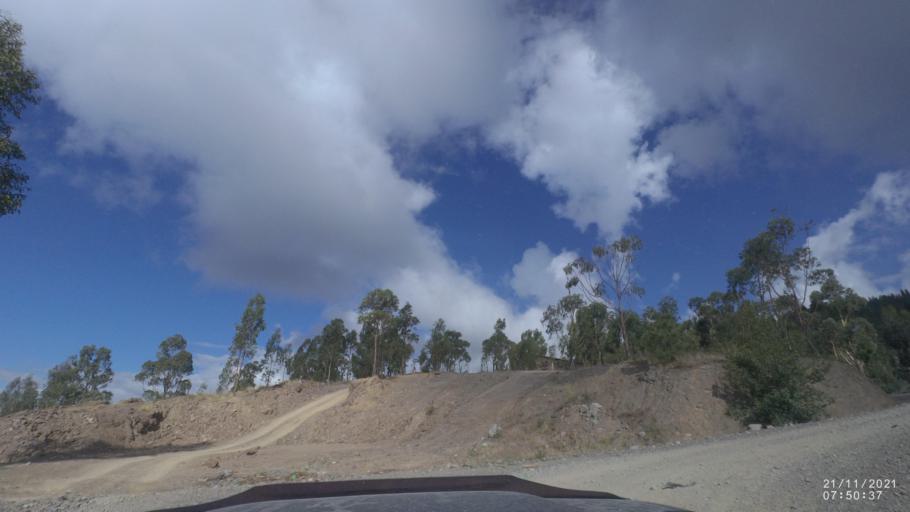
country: BO
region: Cochabamba
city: Cochabamba
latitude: -17.3087
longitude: -66.2161
